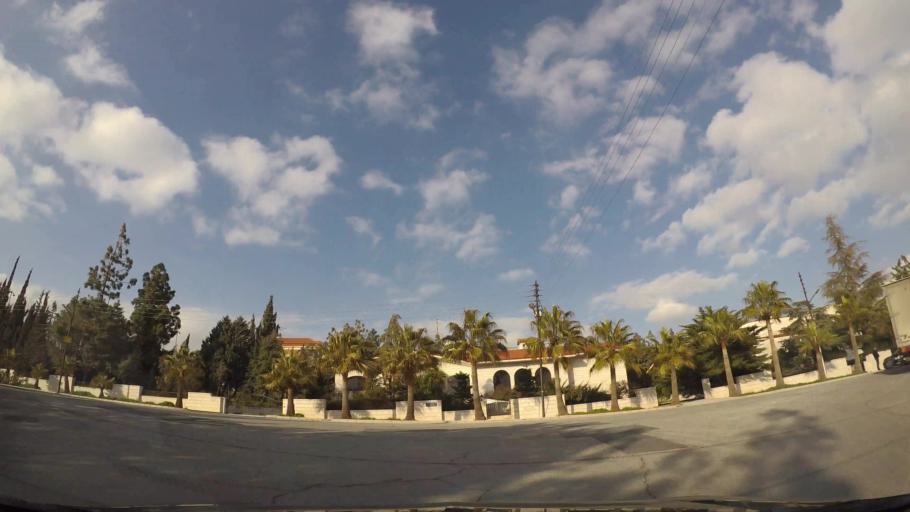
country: JO
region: Amman
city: Al Jubayhah
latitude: 31.9826
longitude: 35.8802
